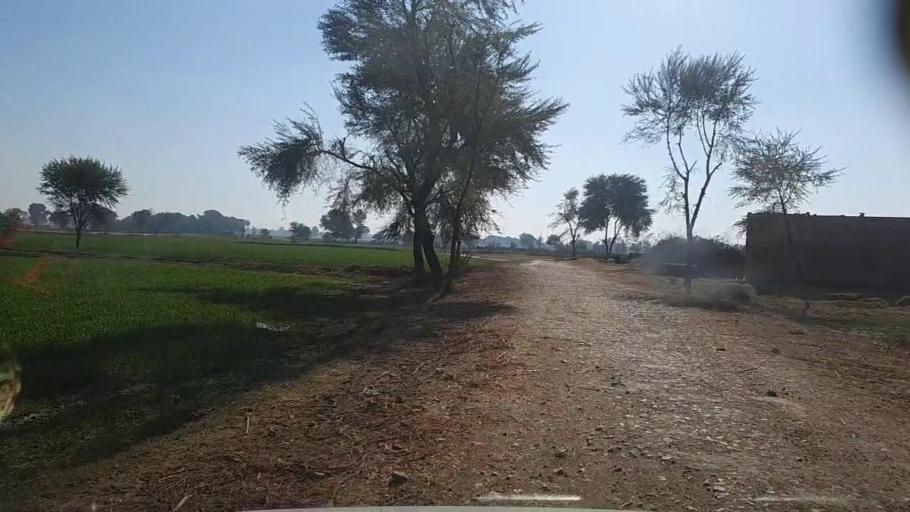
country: PK
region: Sindh
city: Khairpur
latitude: 28.0453
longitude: 69.8205
